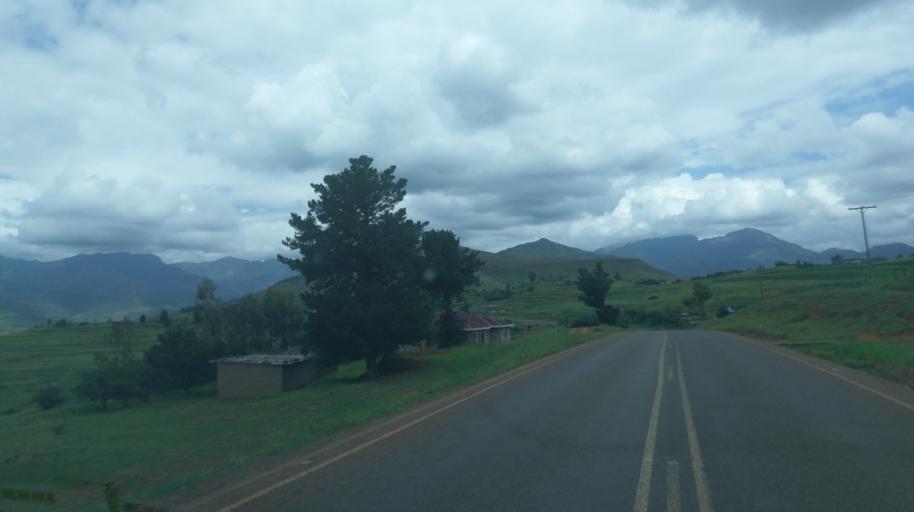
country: LS
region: Leribe
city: Leribe
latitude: -29.0147
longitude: 28.2182
